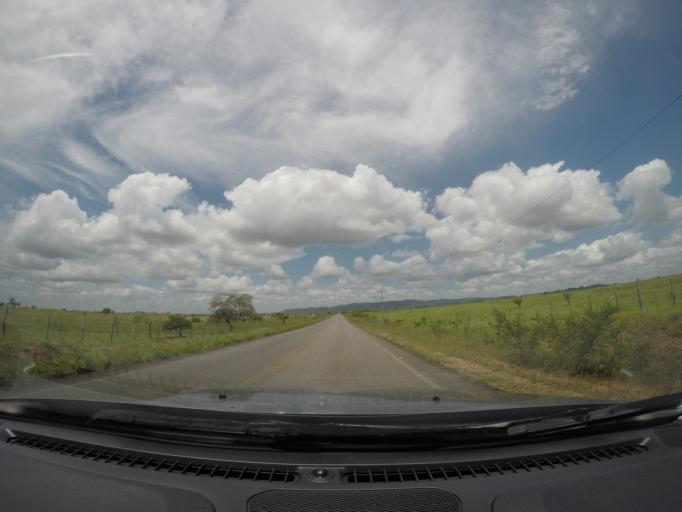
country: BR
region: Bahia
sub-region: Ipira
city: Ipira
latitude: -12.2149
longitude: -39.7839
